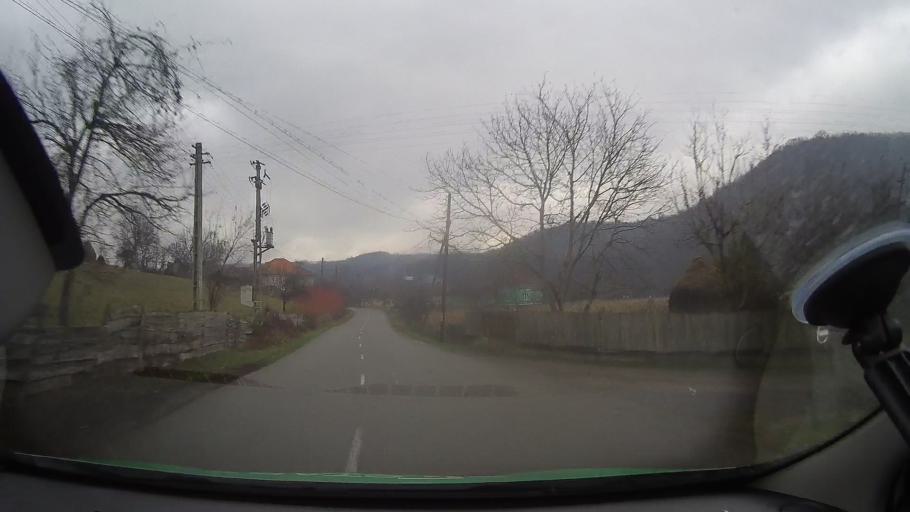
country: RO
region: Hunedoara
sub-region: Comuna Tomesti
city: Tomesti
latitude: 46.1977
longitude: 22.6447
